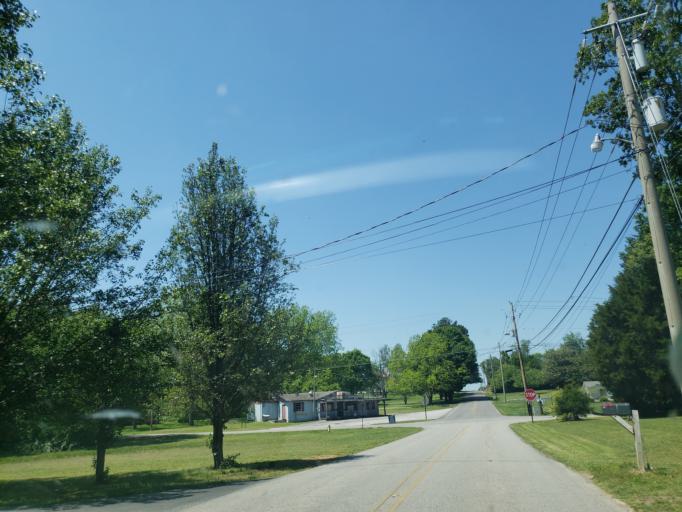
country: US
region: Alabama
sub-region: Madison County
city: Hazel Green
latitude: 34.9621
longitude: -86.6409
